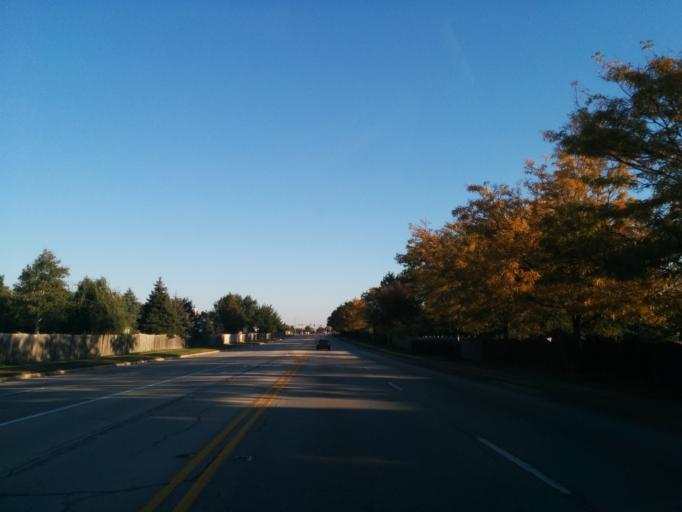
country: US
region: Illinois
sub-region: DuPage County
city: Carol Stream
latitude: 41.9340
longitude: -88.1503
